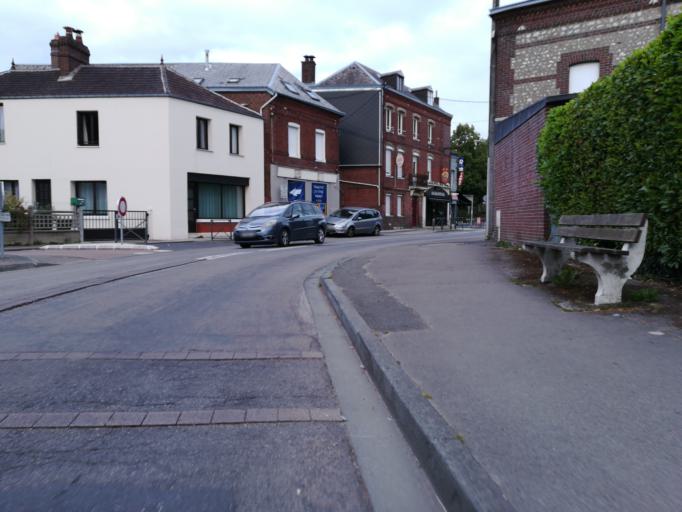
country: FR
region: Haute-Normandie
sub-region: Departement de la Seine-Maritime
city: Mont-Saint-Aignan
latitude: 49.4705
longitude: 1.0821
